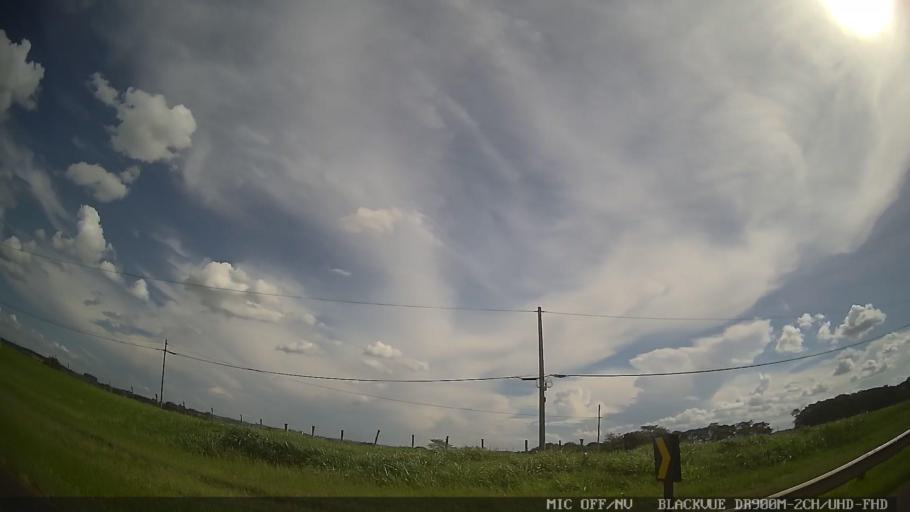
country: BR
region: Sao Paulo
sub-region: Conchas
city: Conchas
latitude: -23.0466
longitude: -47.9563
